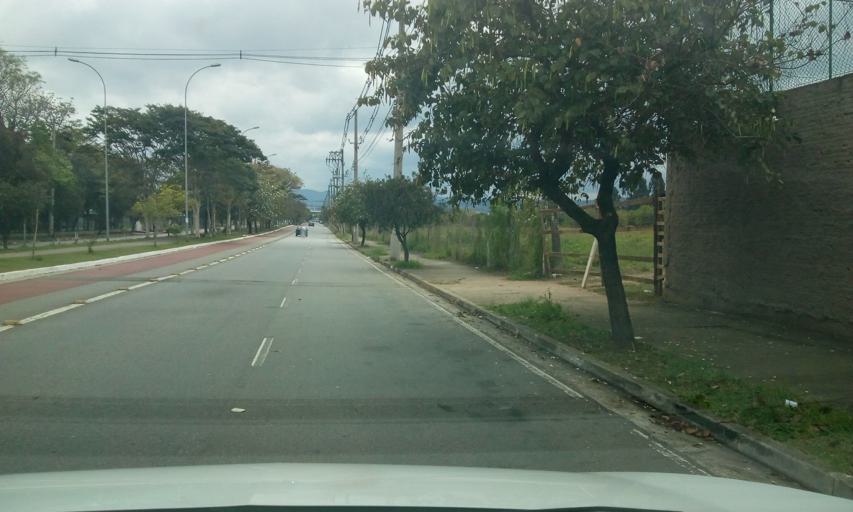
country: BR
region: Sao Paulo
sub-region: Guarulhos
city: Guarulhos
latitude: -23.4563
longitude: -46.4932
